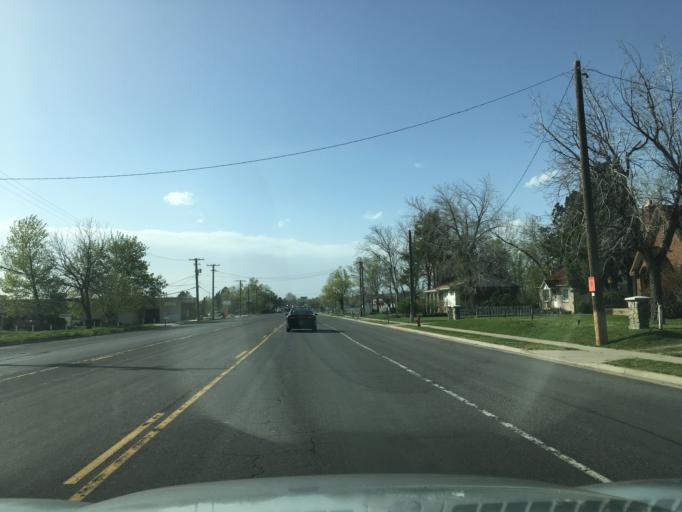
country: US
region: Utah
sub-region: Davis County
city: Kaysville
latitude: 41.0433
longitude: -111.9486
